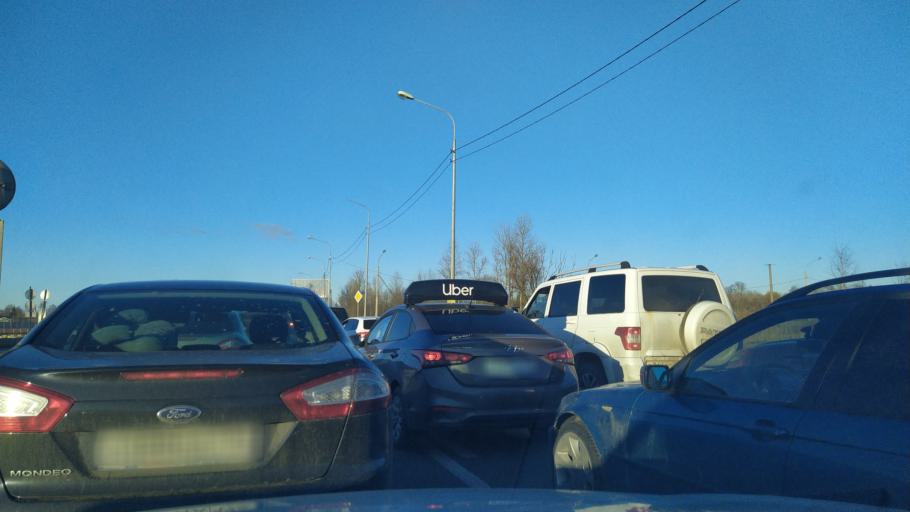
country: RU
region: St.-Petersburg
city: Uritsk
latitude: 59.8104
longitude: 30.1695
